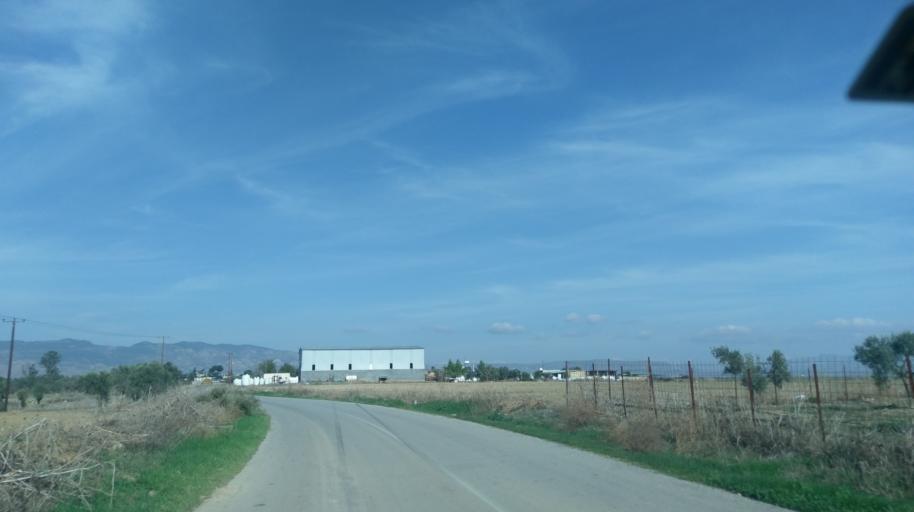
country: CY
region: Ammochostos
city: Lefkonoiko
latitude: 35.2119
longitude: 33.6198
